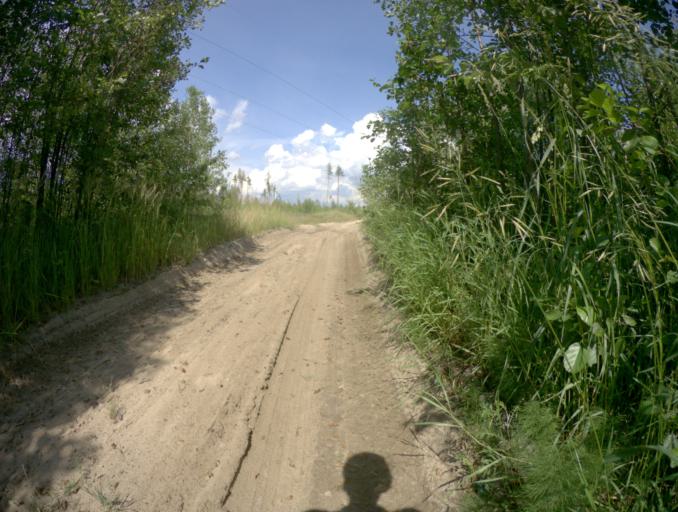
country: RU
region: Ivanovo
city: Talitsy
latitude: 56.5357
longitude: 42.2507
